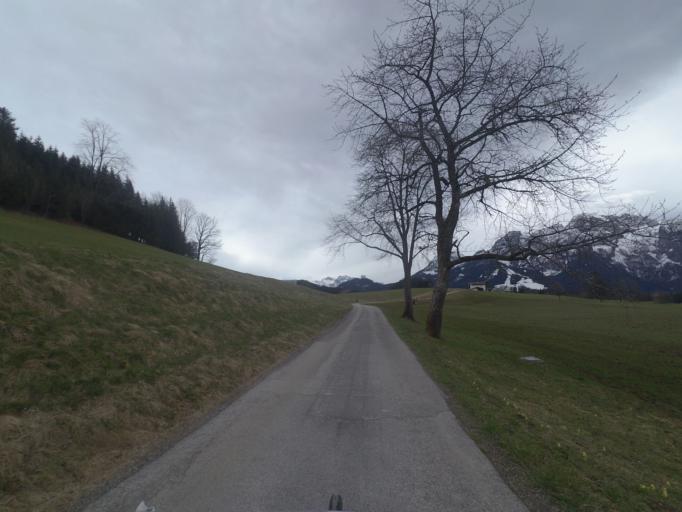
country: AT
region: Salzburg
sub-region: Politischer Bezirk Hallein
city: Abtenau
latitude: 47.5800
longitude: 13.3307
